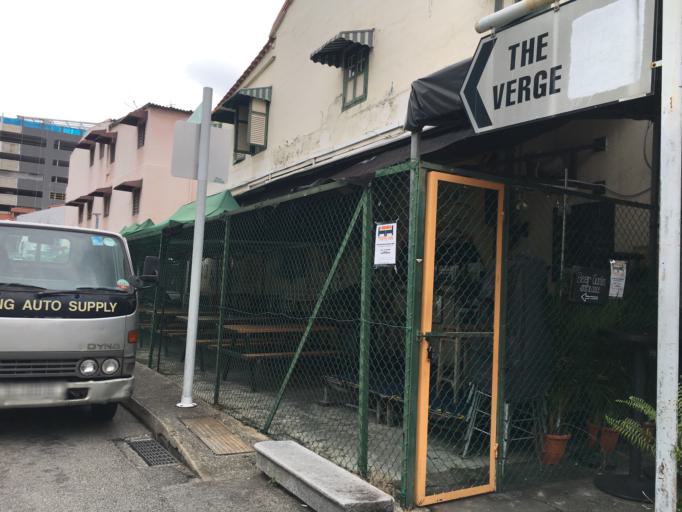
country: SG
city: Singapore
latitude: 1.3053
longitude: 103.8531
